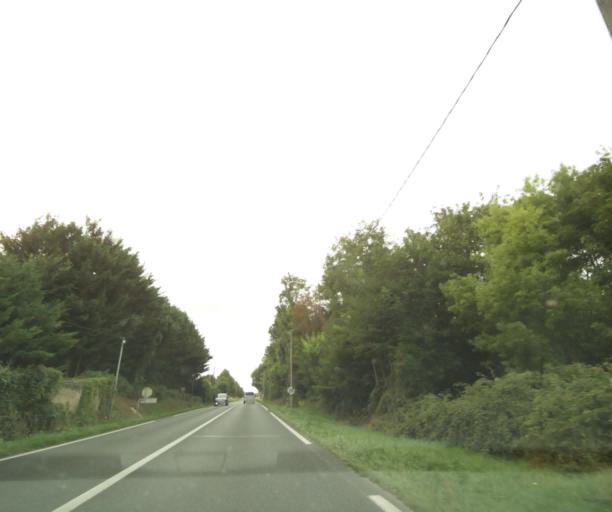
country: FR
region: Centre
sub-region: Departement d'Indre-et-Loire
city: Perrusson
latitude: 47.0774
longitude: 1.0547
